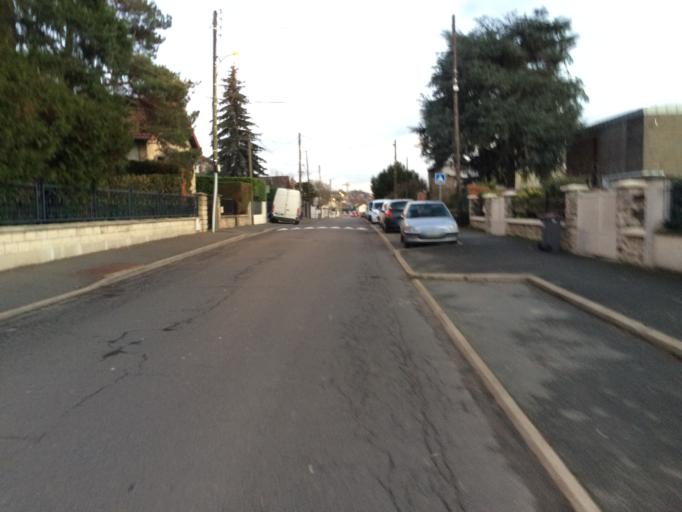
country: FR
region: Ile-de-France
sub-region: Departement de l'Essonne
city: Longjumeau
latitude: 48.6977
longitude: 2.3037
